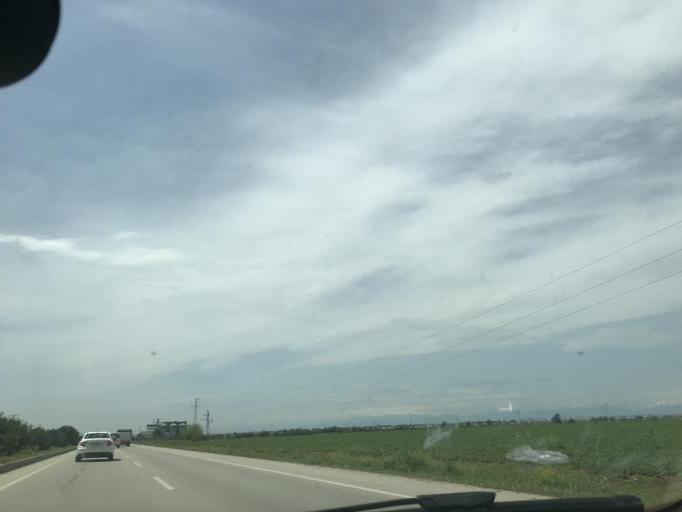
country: TR
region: Adana
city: Yuregir
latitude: 36.9766
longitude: 35.4798
